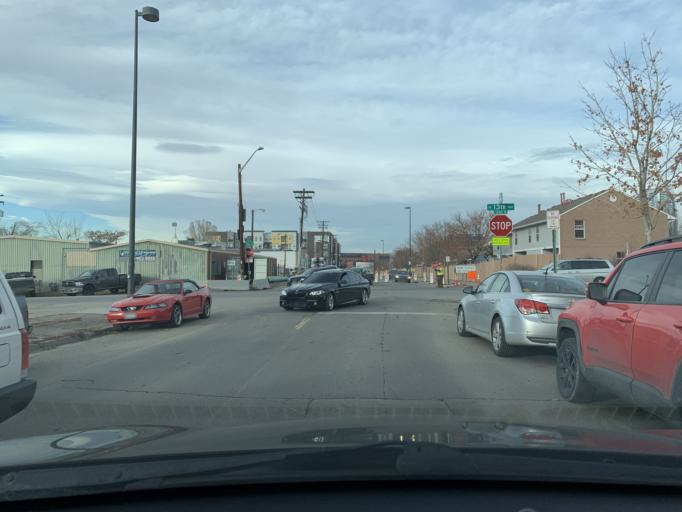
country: US
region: Colorado
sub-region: Denver County
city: Denver
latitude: 39.7367
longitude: -105.0053
